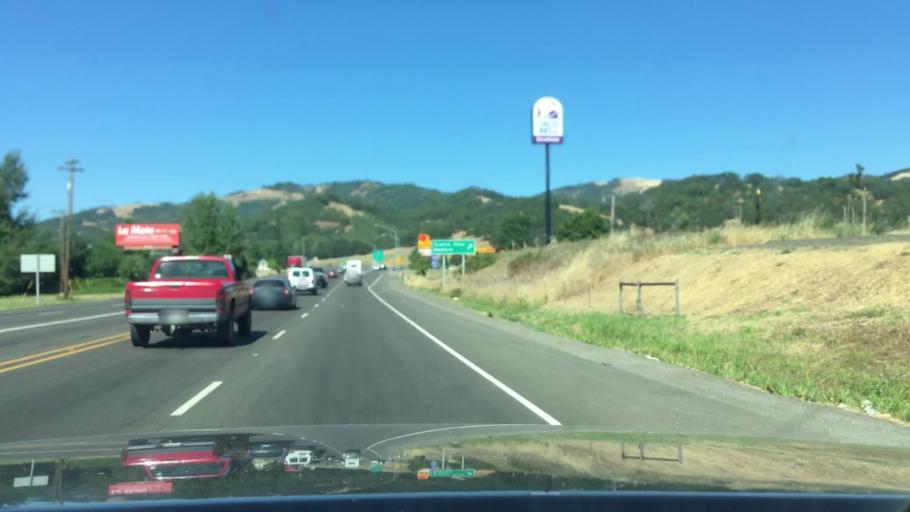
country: US
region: Oregon
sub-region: Douglas County
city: Green
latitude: 43.1498
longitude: -123.3713
